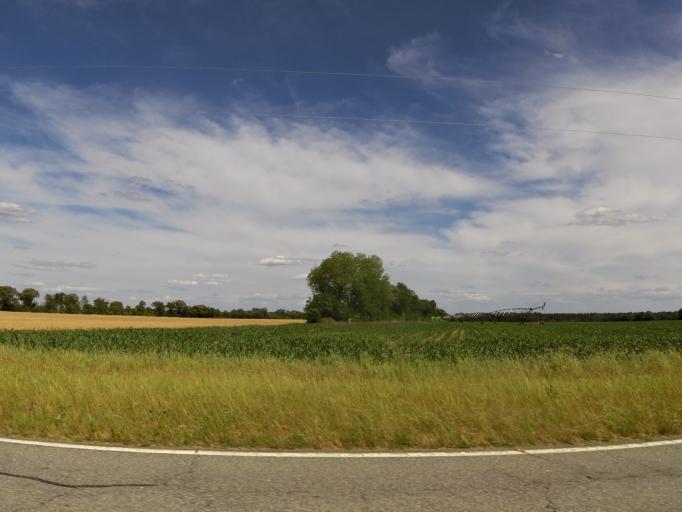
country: US
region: South Carolina
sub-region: Bamberg County
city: Denmark
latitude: 33.1957
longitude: -81.1796
